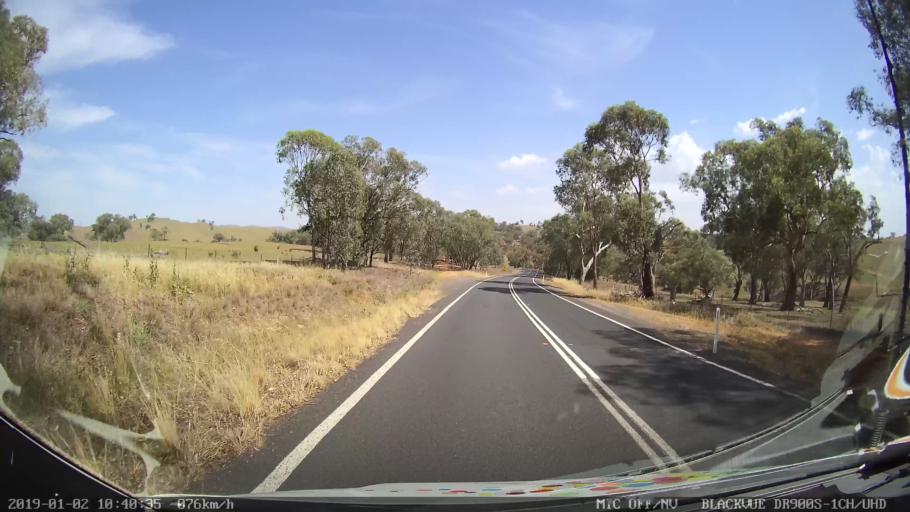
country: AU
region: New South Wales
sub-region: Cootamundra
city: Cootamundra
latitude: -34.8006
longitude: 148.3146
